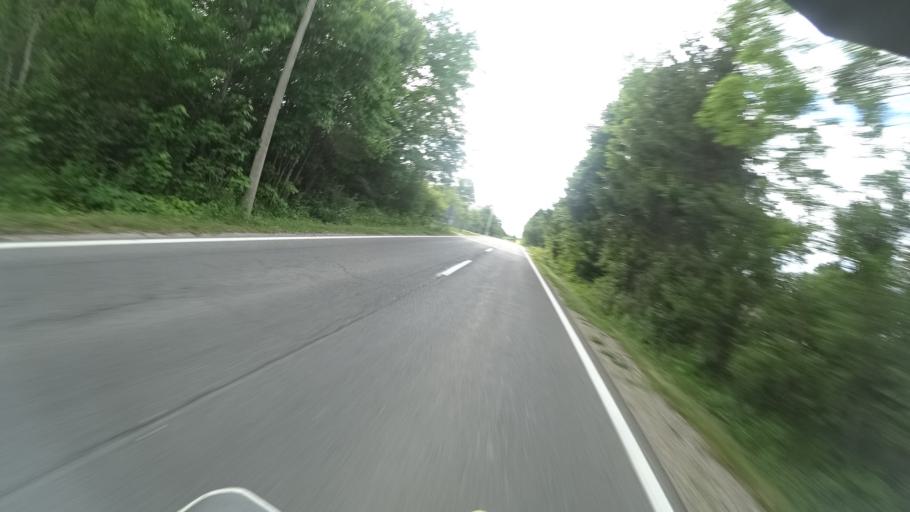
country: HR
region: Licko-Senjska
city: Gospic
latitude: 44.4984
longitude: 15.4561
